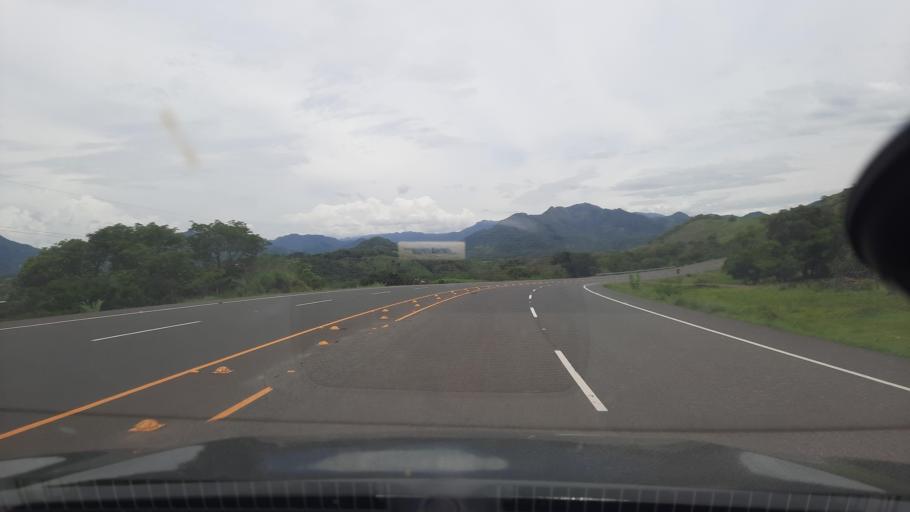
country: HN
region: Valle
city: Aramecina
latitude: 13.7933
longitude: -87.7043
